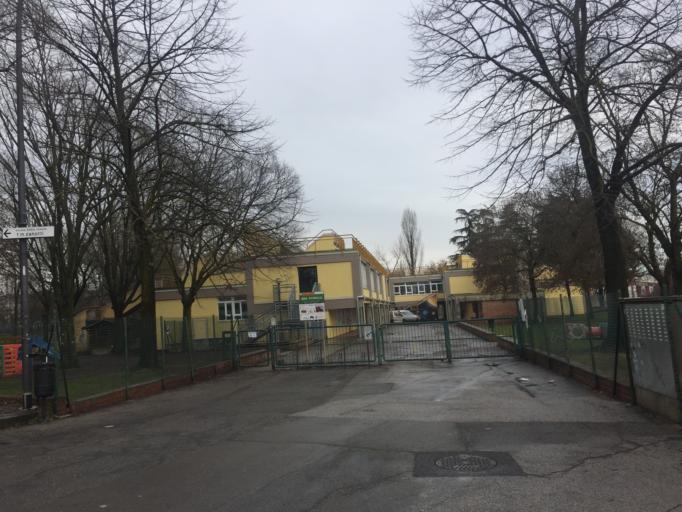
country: IT
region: Emilia-Romagna
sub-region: Provincia di Bologna
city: Bologna
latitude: 44.5104
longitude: 11.3048
